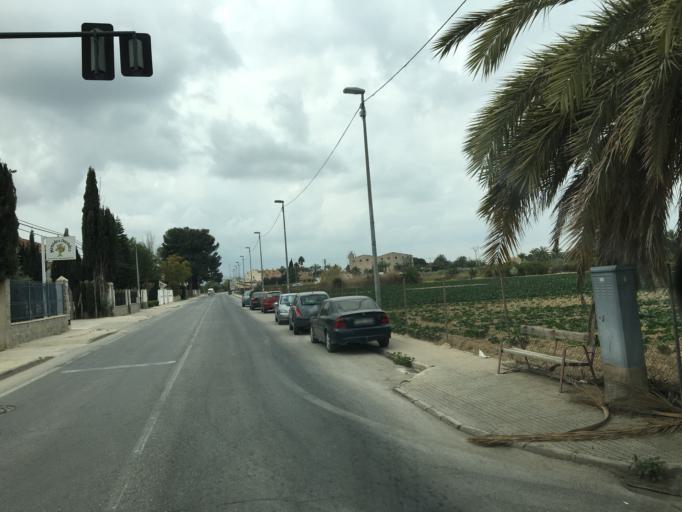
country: ES
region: Murcia
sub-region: Murcia
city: Beniel
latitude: 38.0235
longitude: -1.0316
